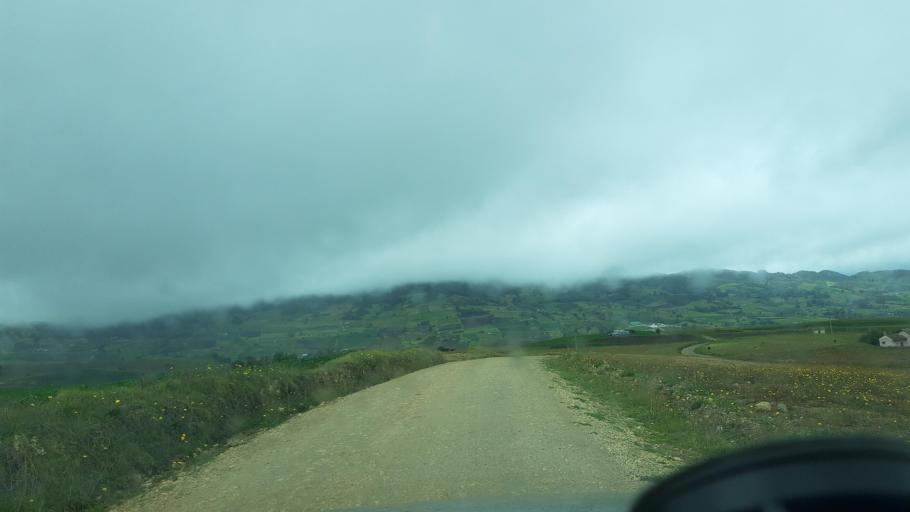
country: CO
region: Boyaca
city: Cucaita
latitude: 5.5216
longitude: -73.4381
